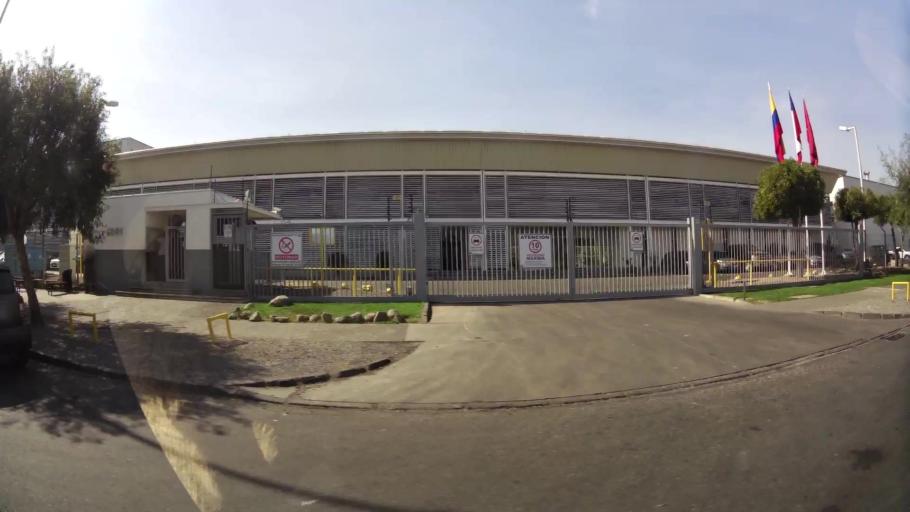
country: CL
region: Santiago Metropolitan
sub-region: Provincia de Santiago
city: Lo Prado
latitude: -33.4263
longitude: -70.7741
